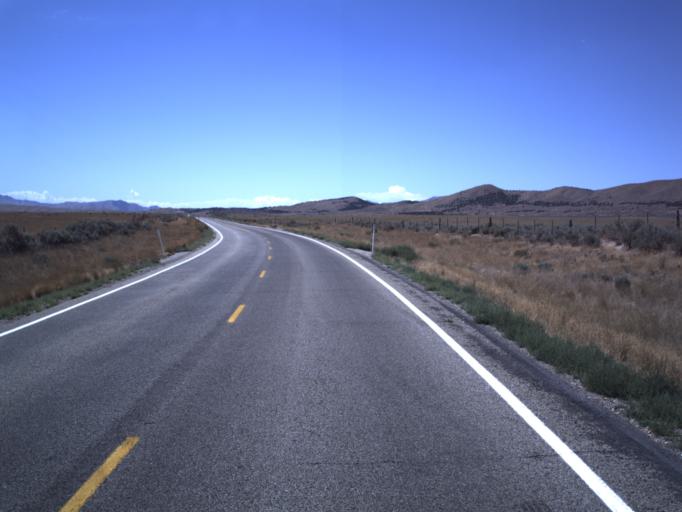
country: US
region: Utah
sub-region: Juab County
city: Nephi
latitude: 39.6958
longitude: -111.9915
